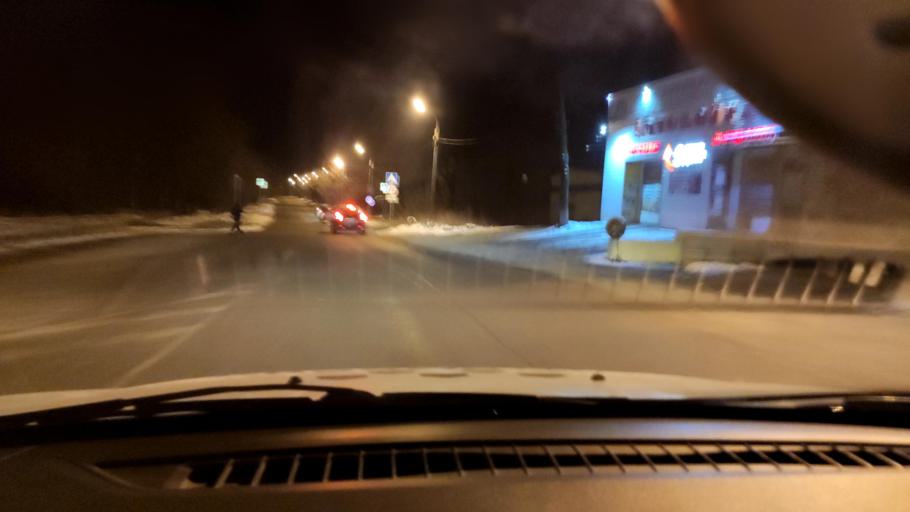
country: RU
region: Perm
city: Kultayevo
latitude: 57.9951
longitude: 55.9308
